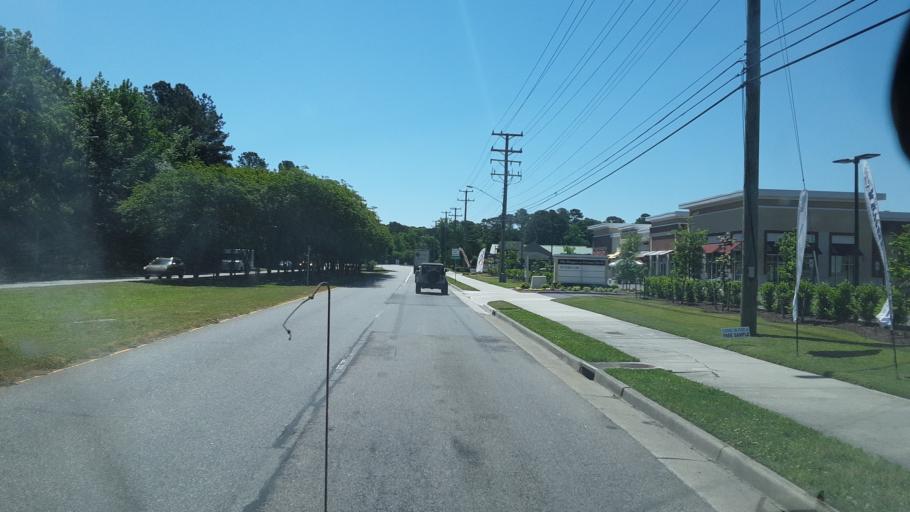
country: US
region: Virginia
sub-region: City of Virginia Beach
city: Virginia Beach
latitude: 36.7949
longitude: -75.9993
